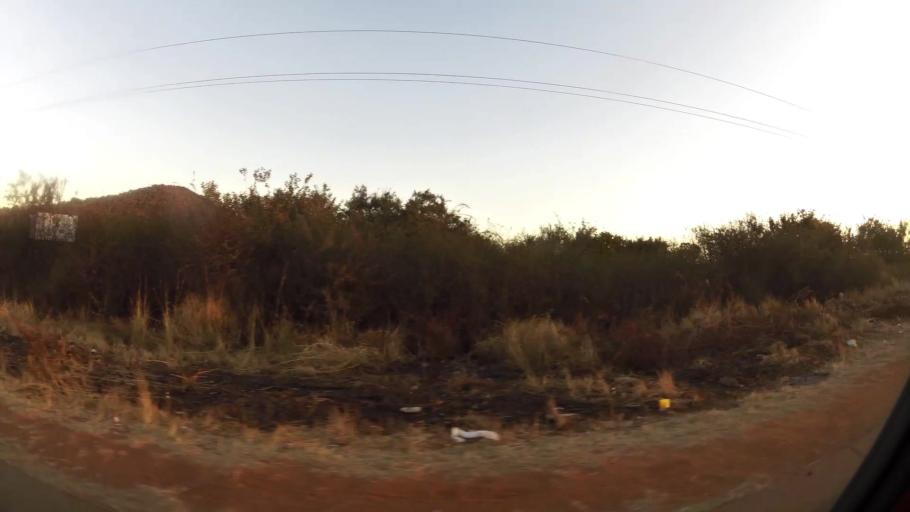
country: ZA
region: North-West
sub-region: Bojanala Platinum District Municipality
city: Rustenburg
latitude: -25.6073
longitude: 27.1830
